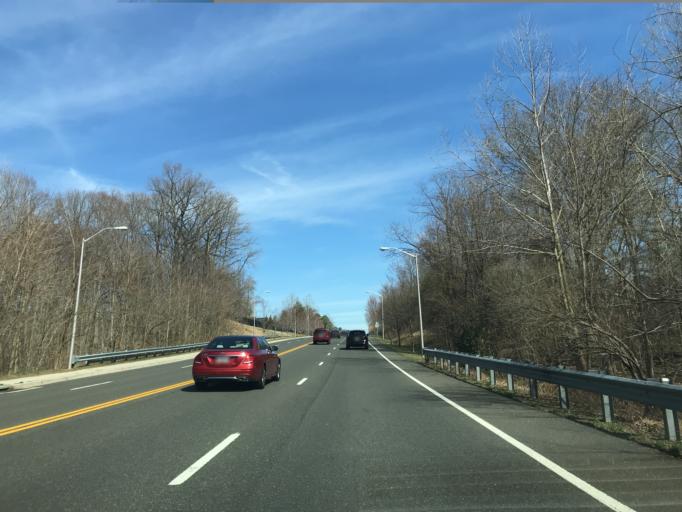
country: US
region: Maryland
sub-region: Prince George's County
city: Woodmore
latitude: 38.9200
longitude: -76.8105
